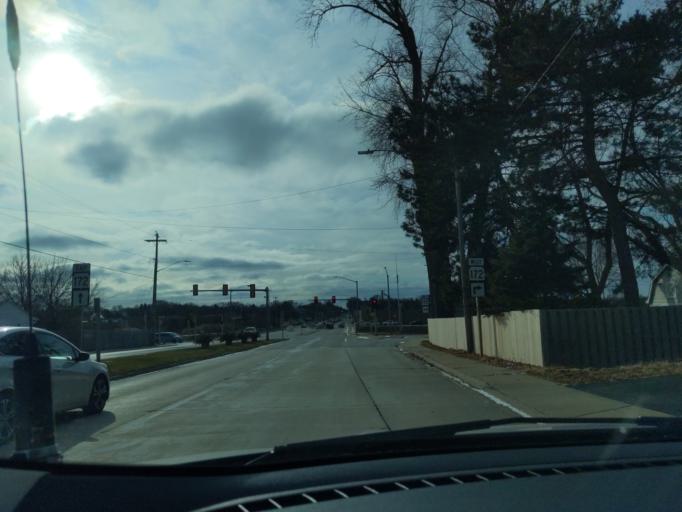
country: US
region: Wisconsin
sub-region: Brown County
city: Allouez
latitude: 44.4718
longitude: -88.0307
